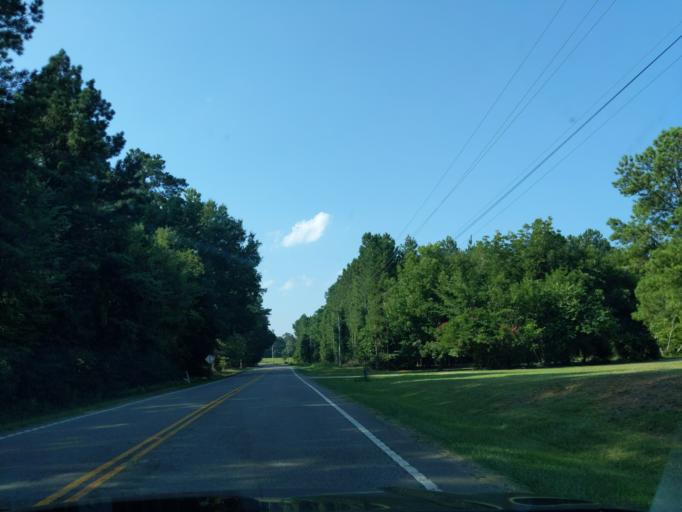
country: US
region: South Carolina
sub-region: Newberry County
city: Prosperity
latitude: 34.0664
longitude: -81.5608
